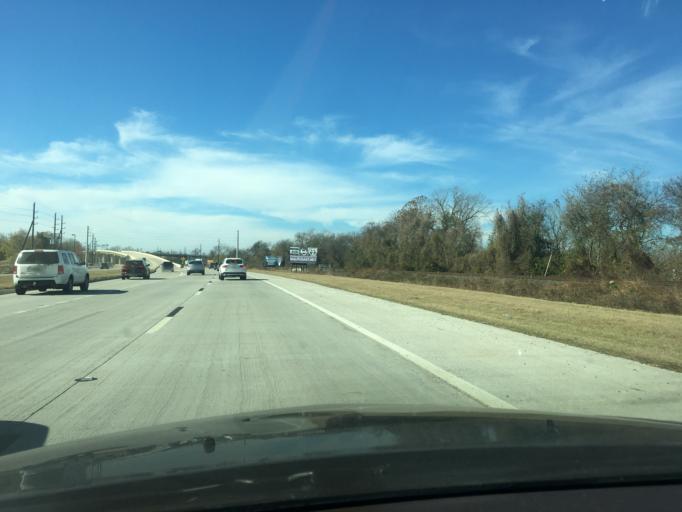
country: US
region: Texas
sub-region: Fort Bend County
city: Richmond
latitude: 29.5963
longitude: -95.7364
